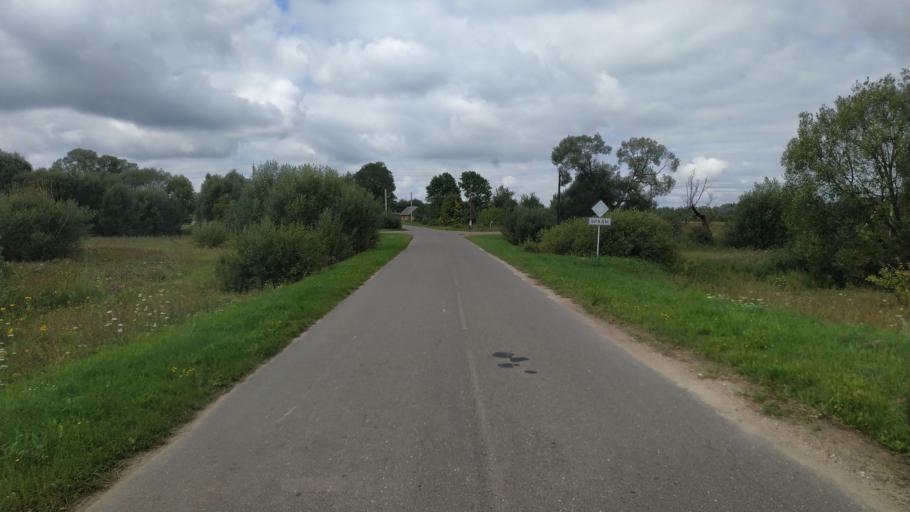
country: BY
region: Mogilev
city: Chavusy
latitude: 53.7802
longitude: 30.8900
